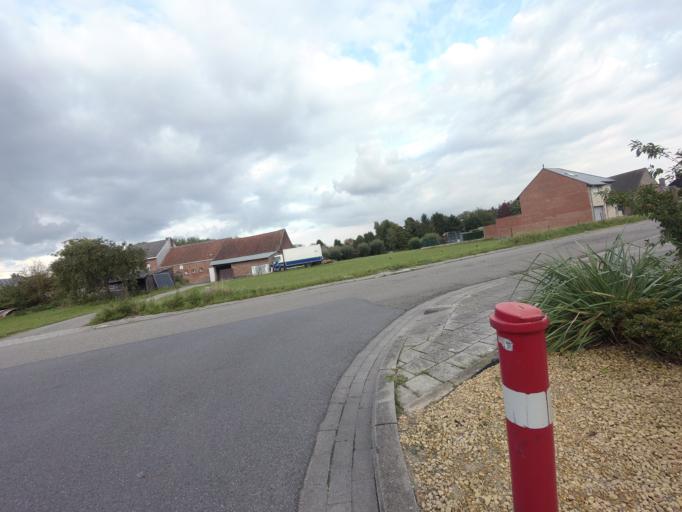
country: BE
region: Flanders
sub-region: Provincie Vlaams-Brabant
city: Kapelle-op-den-Bos
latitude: 51.0165
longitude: 4.3520
